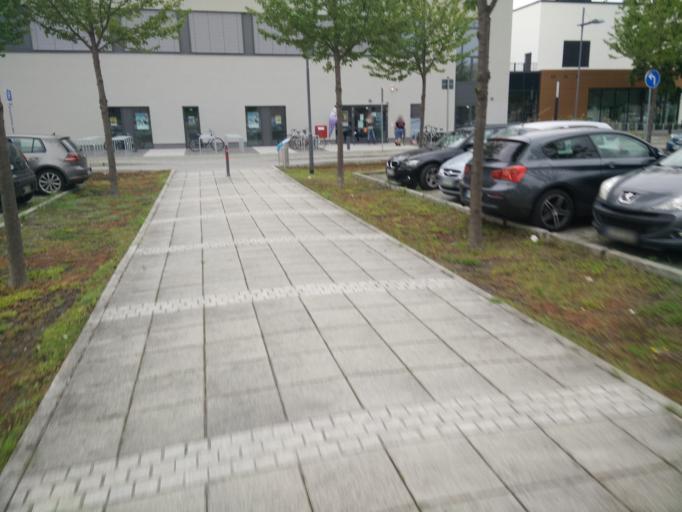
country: DE
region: Brandenburg
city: Falkensee
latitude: 52.5619
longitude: 13.0907
